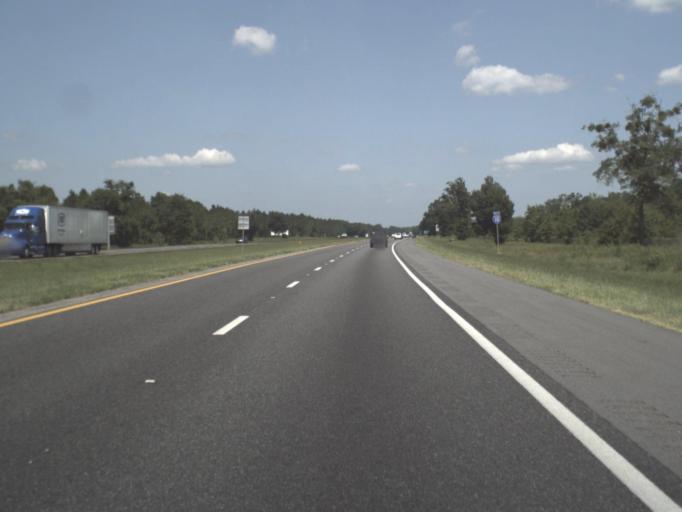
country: US
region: Florida
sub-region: Madison County
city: Madison
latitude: 30.3818
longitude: -83.3059
